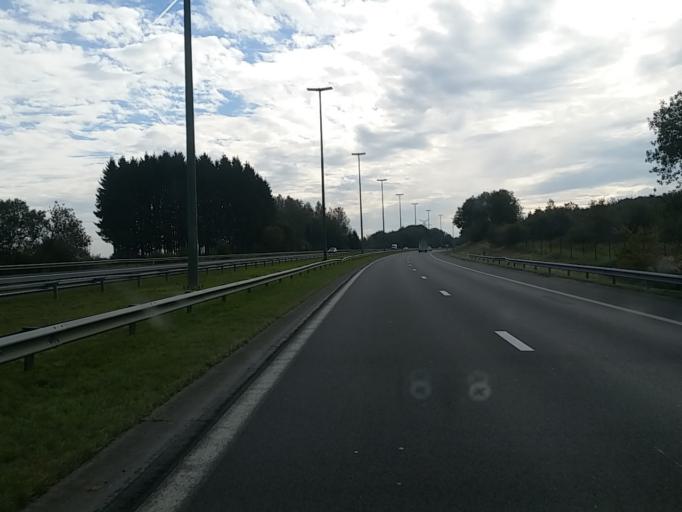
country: BE
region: Wallonia
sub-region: Province du Luxembourg
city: Arlon
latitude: 49.6882
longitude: 5.7438
